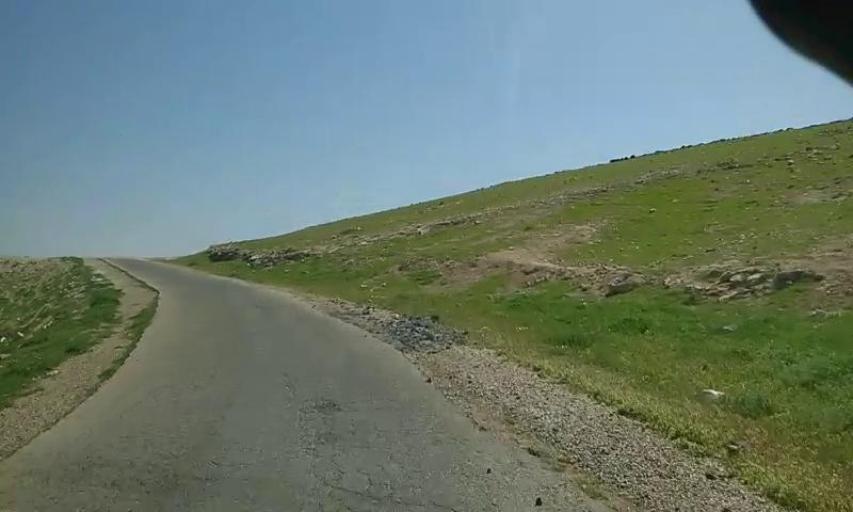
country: PS
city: `Arab ar Rashaydah
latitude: 31.5579
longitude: 35.2470
